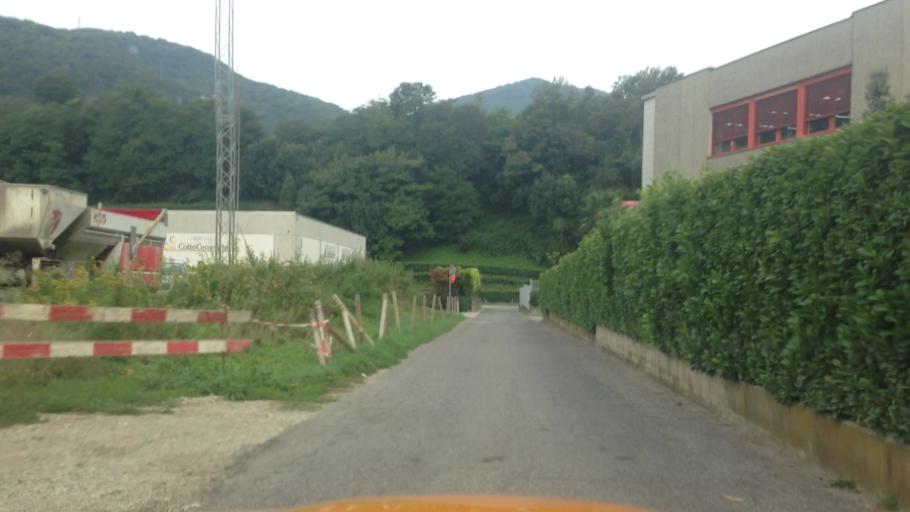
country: CH
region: Ticino
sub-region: Mendrisio District
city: Mendrisio
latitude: 45.8808
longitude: 8.9785
